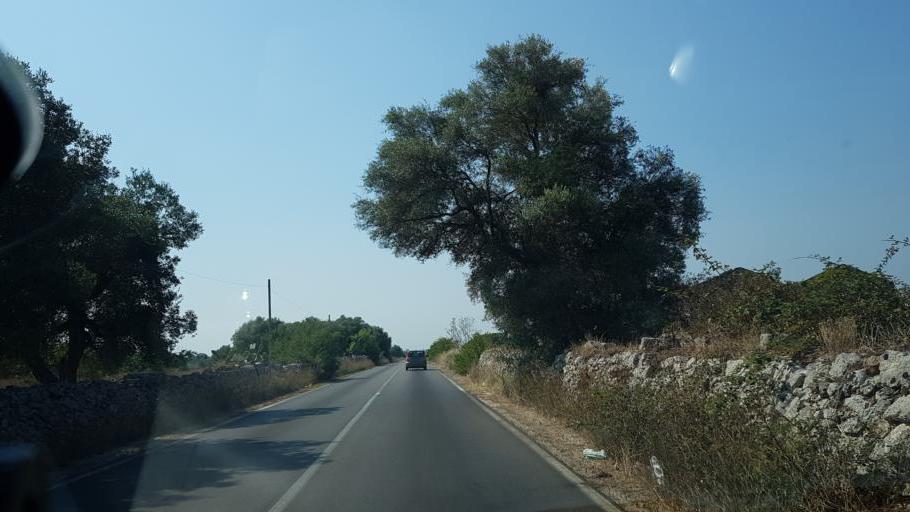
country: IT
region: Apulia
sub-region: Provincia di Taranto
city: Manduria
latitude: 40.4498
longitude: 17.6370
